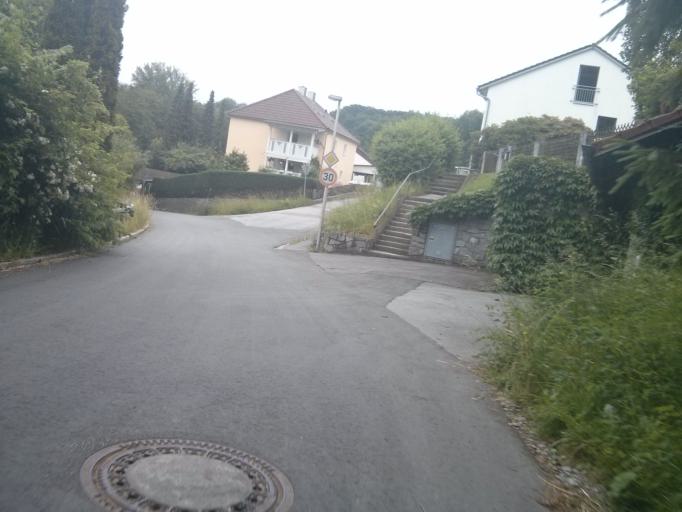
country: DE
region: Bavaria
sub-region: Lower Bavaria
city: Deggendorf
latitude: 48.8416
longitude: 12.9660
